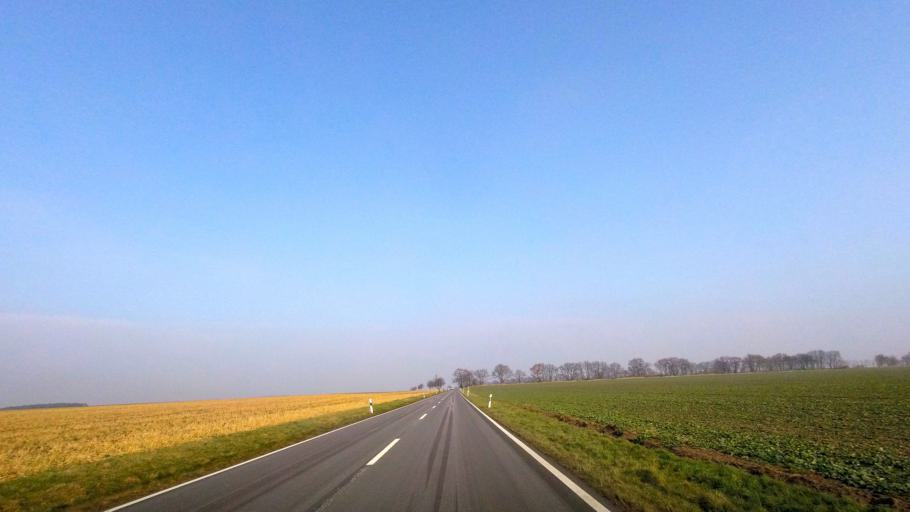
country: DE
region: Brandenburg
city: Niedergorsdorf
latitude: 51.9392
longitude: 13.0372
